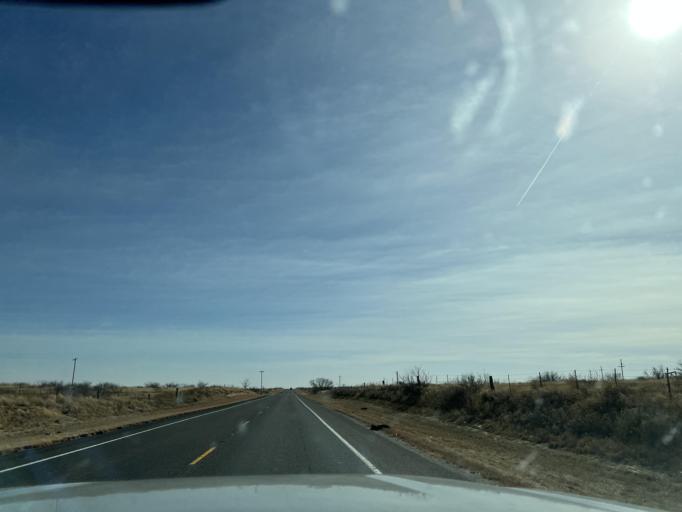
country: US
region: Texas
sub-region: Andrews County
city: Andrews
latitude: 32.4724
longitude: -102.4666
